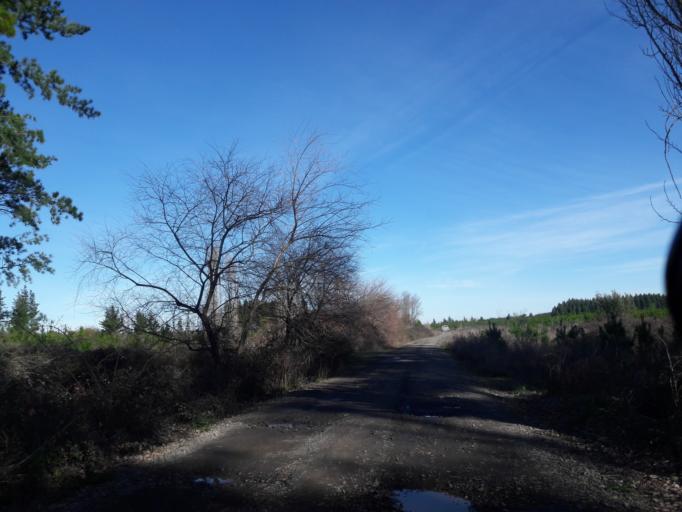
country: CL
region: Biobio
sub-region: Provincia de Biobio
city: Cabrero
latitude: -37.0137
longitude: -72.1874
